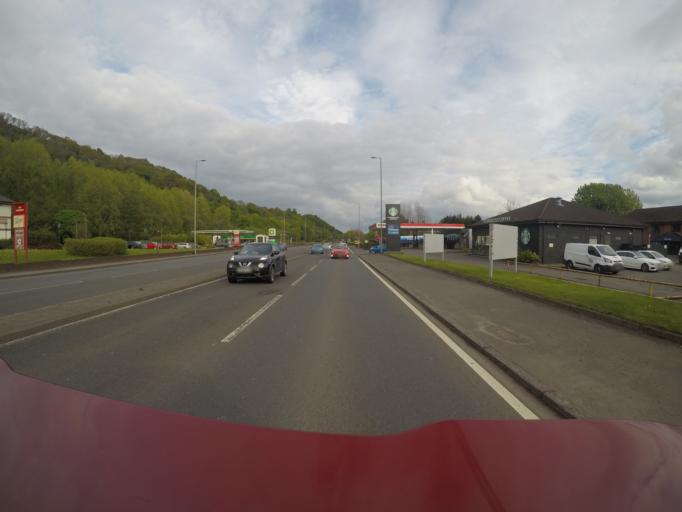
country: GB
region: Scotland
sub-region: Renfrewshire
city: Bishopton
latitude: 55.9359
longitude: -4.5169
